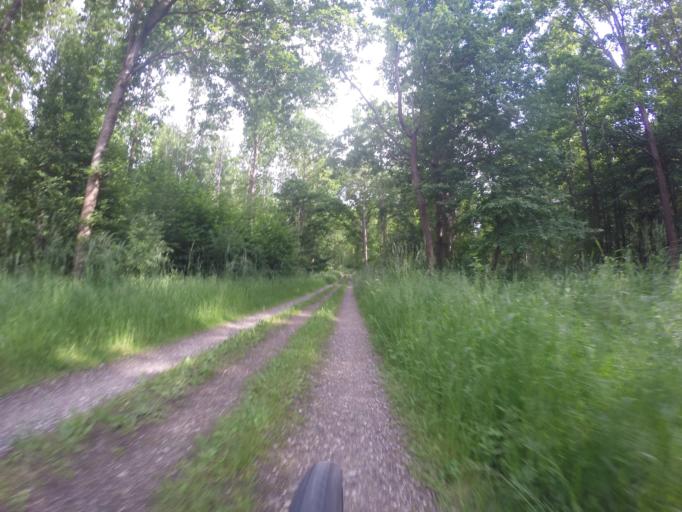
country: DK
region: Capital Region
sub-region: Ballerup Kommune
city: Ballerup
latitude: 55.6999
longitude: 12.3476
